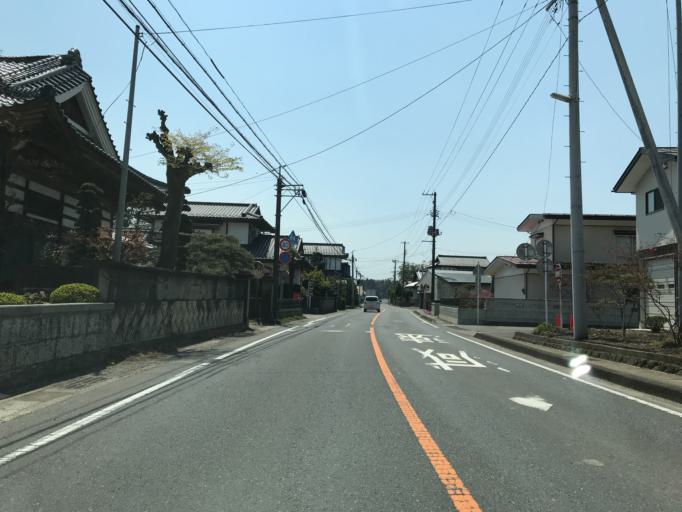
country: JP
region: Fukushima
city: Ishikawa
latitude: 37.1270
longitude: 140.3504
